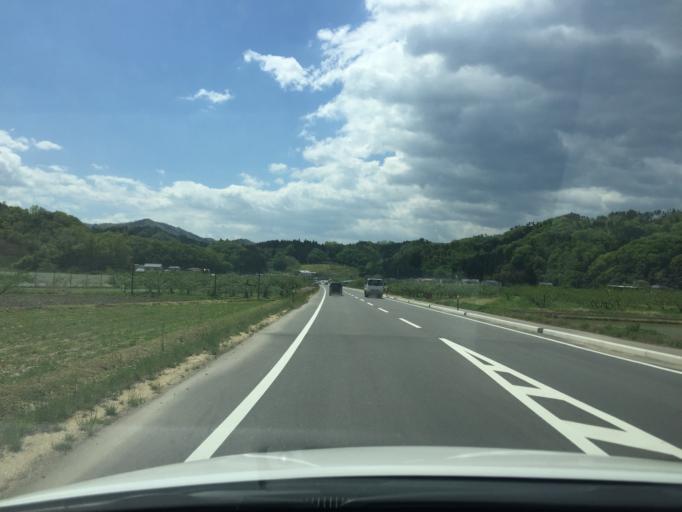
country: JP
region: Fukushima
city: Hobaramachi
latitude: 37.7486
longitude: 140.6072
